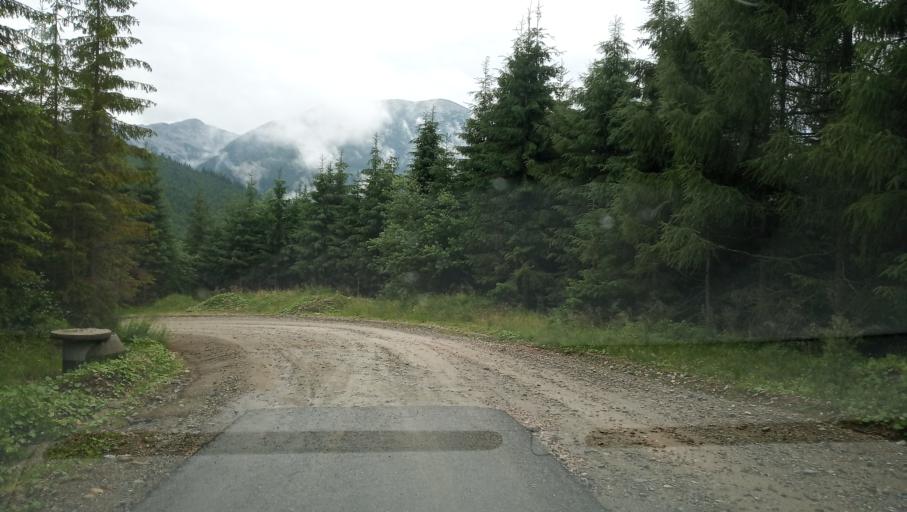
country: RO
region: Hunedoara
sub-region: Oras Petrila
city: Petrila
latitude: 45.4044
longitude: 23.5739
